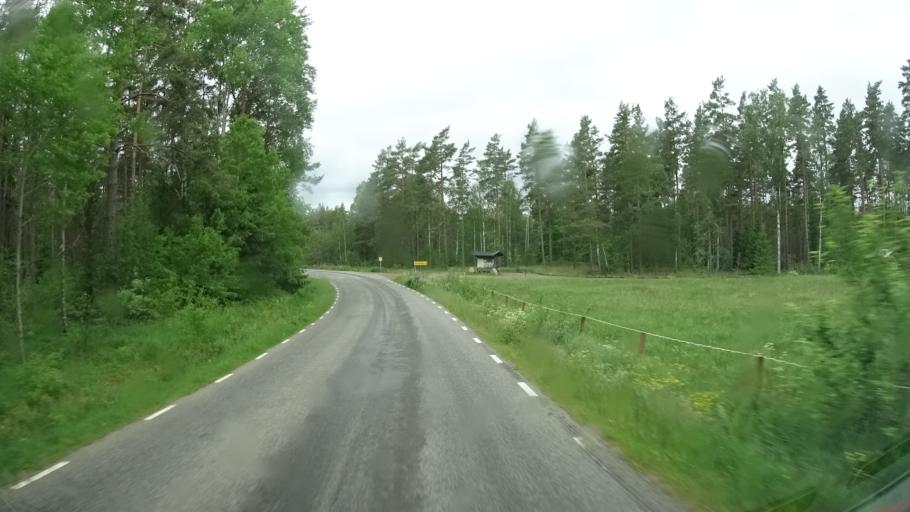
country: SE
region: Joenkoeping
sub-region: Eksjo Kommun
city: Mariannelund
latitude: 57.7033
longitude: 15.6346
